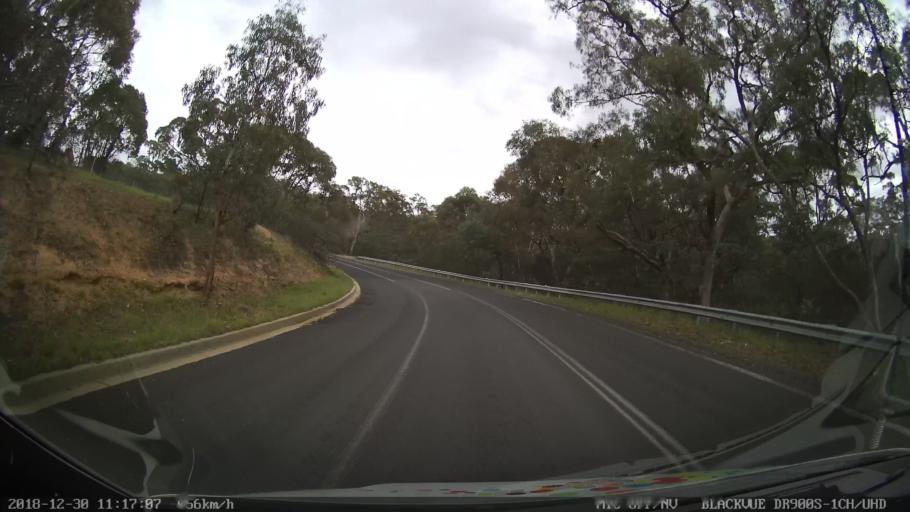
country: AU
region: New South Wales
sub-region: Snowy River
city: Jindabyne
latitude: -36.5362
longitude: 148.7015
